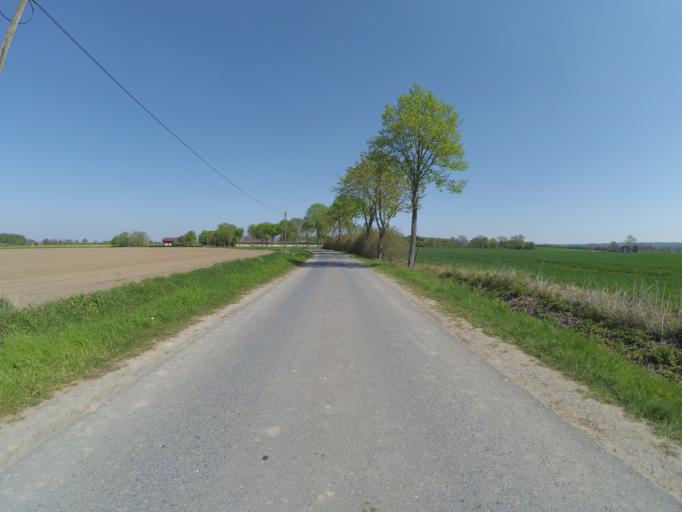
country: DE
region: North Rhine-Westphalia
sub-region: Regierungsbezirk Munster
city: Nordkirchen
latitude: 51.7665
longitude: 7.5461
